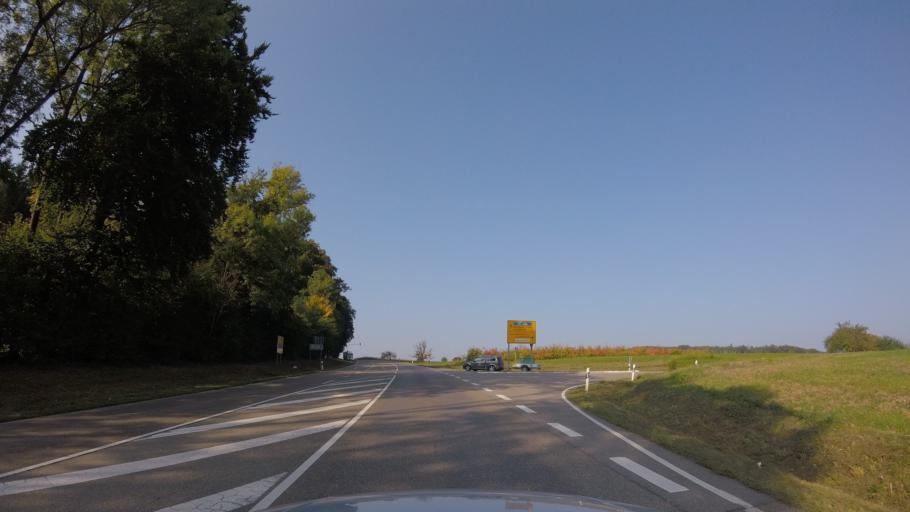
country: DE
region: Baden-Wuerttemberg
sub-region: Regierungsbezirk Stuttgart
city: Mundelsheim
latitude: 49.0077
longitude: 9.2488
